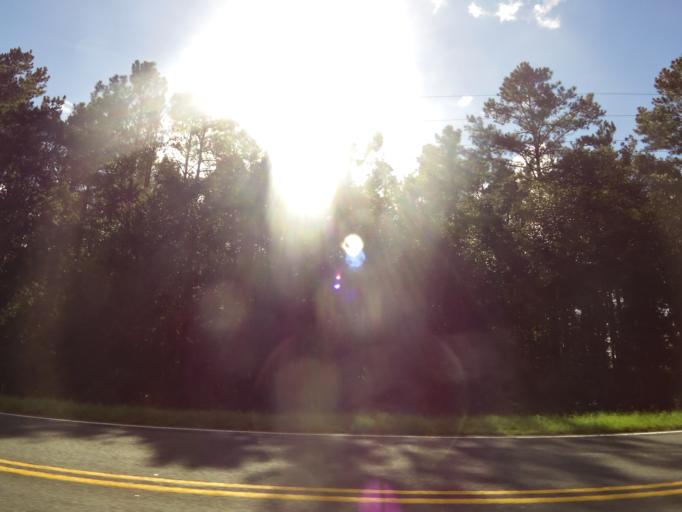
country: US
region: Georgia
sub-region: Camden County
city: Woodbine
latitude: 31.0031
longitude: -81.7320
